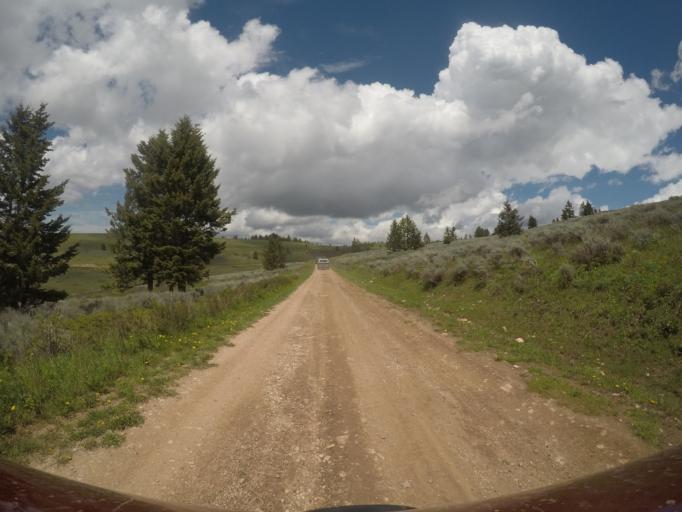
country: US
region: Wyoming
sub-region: Big Horn County
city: Lovell
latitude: 45.1785
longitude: -108.4372
